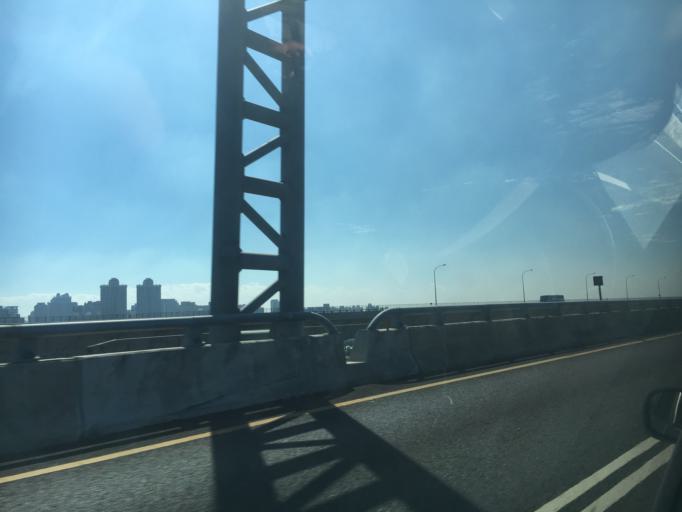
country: TW
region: Taiwan
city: Taoyuan City
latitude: 25.0358
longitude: 121.2936
